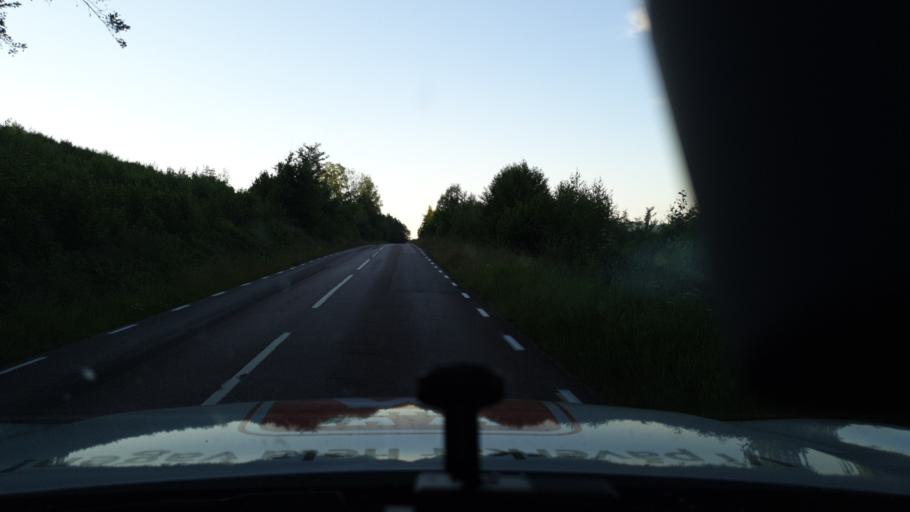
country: SE
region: Vaermland
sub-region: Kils Kommun
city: Kil
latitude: 59.5913
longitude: 13.3143
